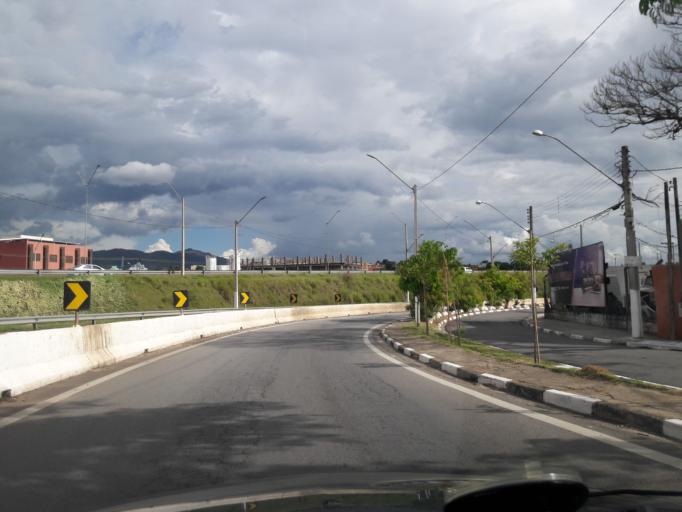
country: BR
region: Sao Paulo
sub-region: Atibaia
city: Atibaia
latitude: -23.1137
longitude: -46.5724
